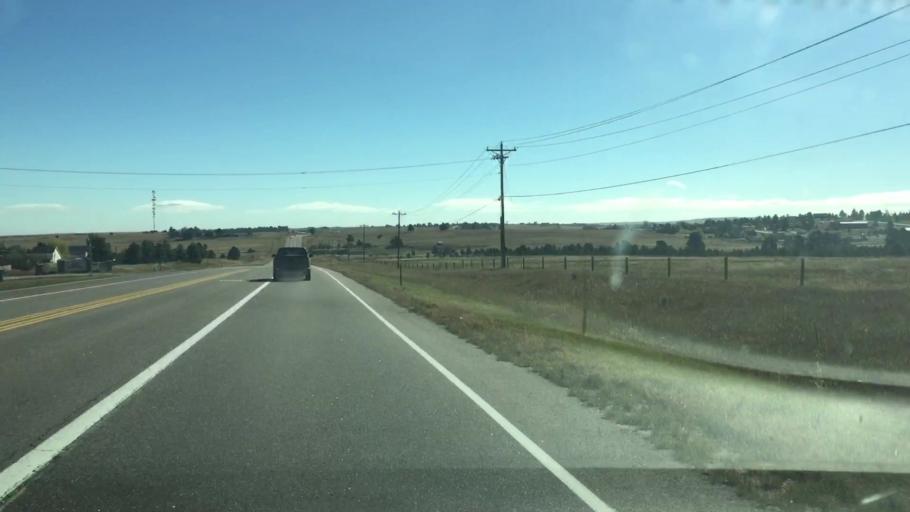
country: US
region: Colorado
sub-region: Elbert County
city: Elizabeth
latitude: 39.3613
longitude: -104.5599
